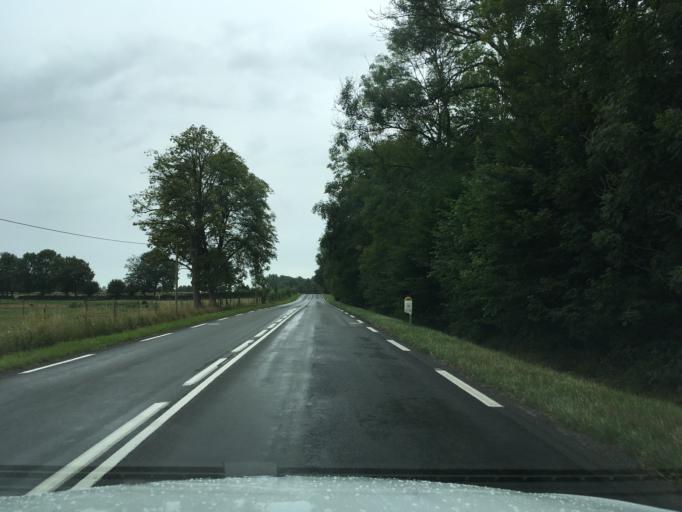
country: FR
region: Picardie
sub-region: Departement de l'Aisne
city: Esqueheries
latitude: 49.9471
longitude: 3.7693
